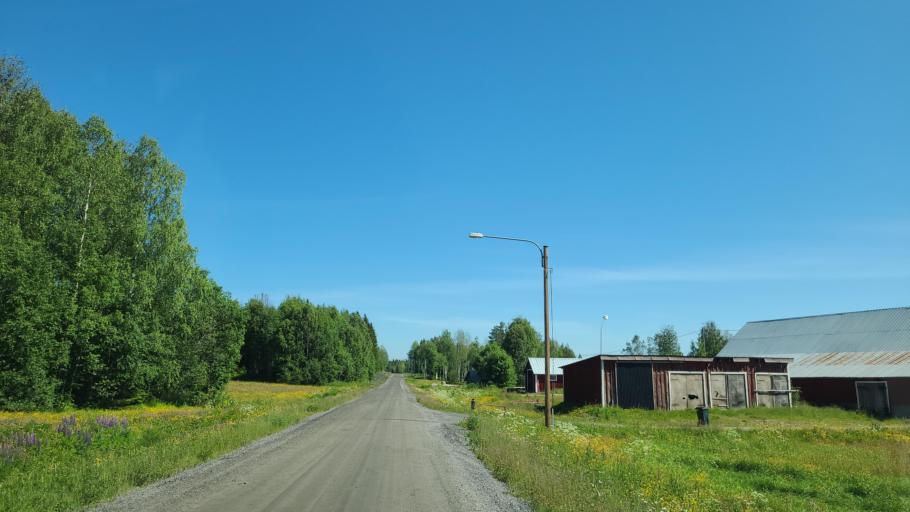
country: SE
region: Vaesterbotten
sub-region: Bjurholms Kommun
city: Bjurholm
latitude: 63.6412
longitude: 19.1349
